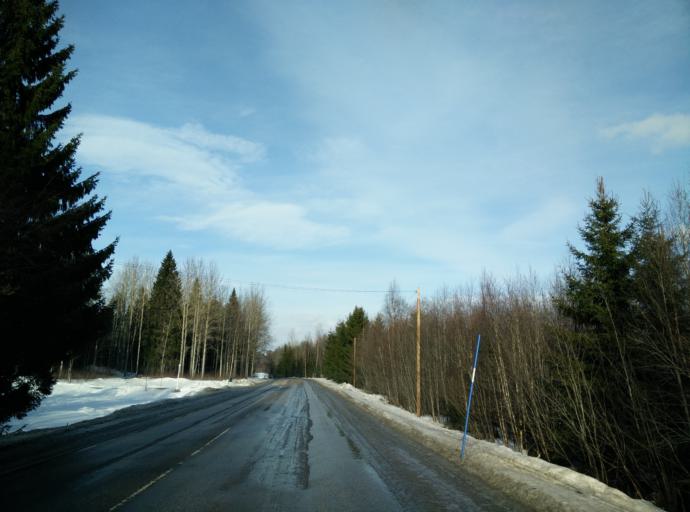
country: SE
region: Vaesternorrland
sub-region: Sundsvalls Kommun
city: Njurundabommen
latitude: 62.2379
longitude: 17.3825
